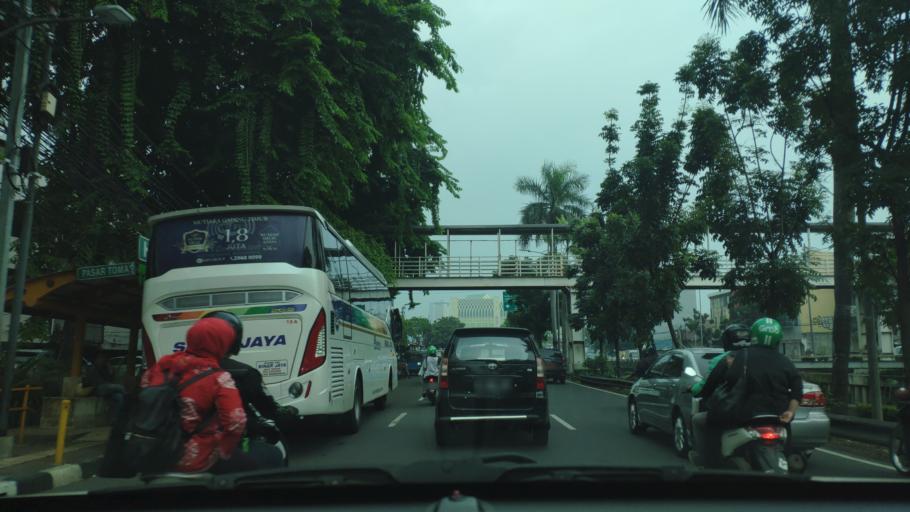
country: ID
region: Jakarta Raya
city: Jakarta
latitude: -6.1791
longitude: 106.8130
